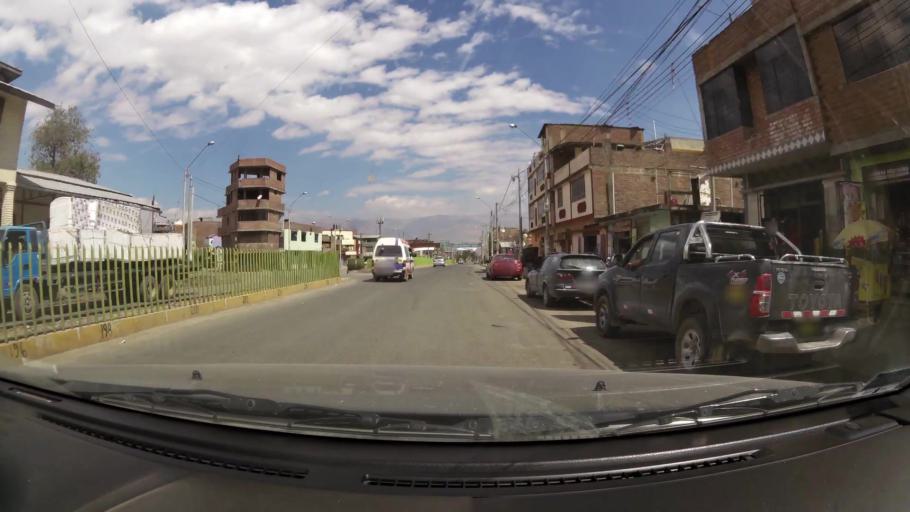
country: PE
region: Junin
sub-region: Provincia de Huancayo
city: Huancayo
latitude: -12.0791
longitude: -75.2076
